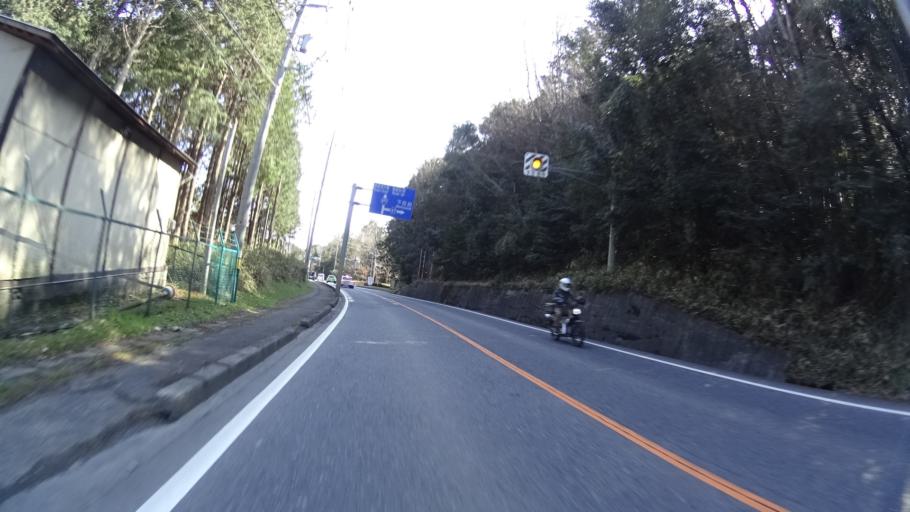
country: JP
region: Shiga Prefecture
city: Kitahama
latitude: 35.1519
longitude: 135.8760
